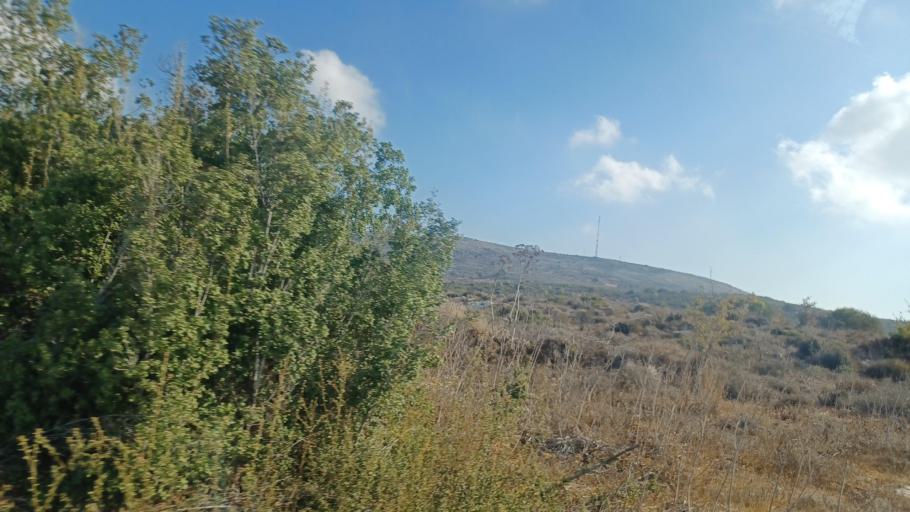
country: CY
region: Pafos
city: Mesogi
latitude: 34.7788
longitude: 32.4680
